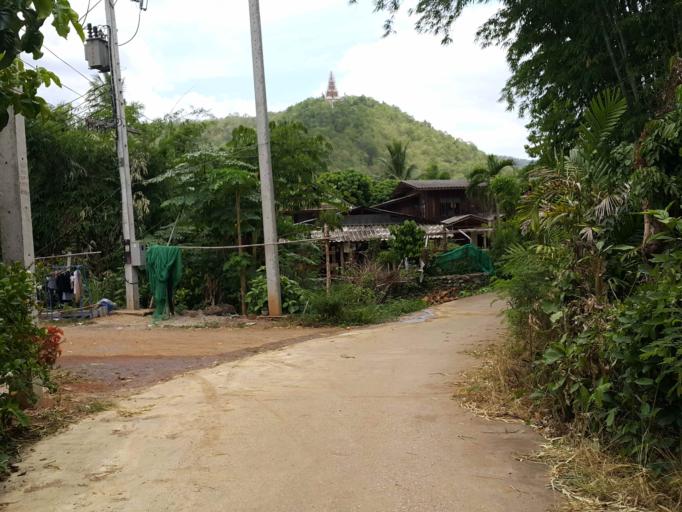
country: TH
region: Chiang Mai
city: Hang Dong
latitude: 18.7503
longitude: 98.8877
